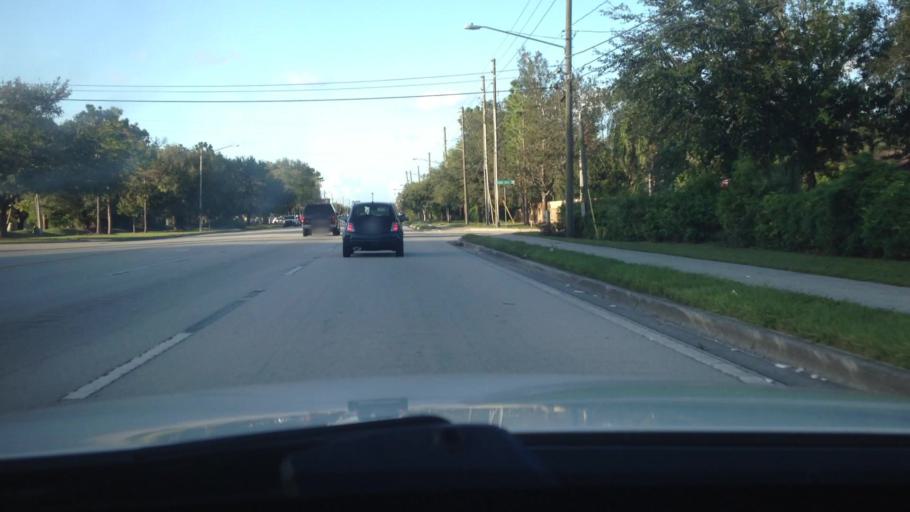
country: US
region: Florida
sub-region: Orange County
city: Union Park
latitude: 28.5591
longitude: -81.2859
